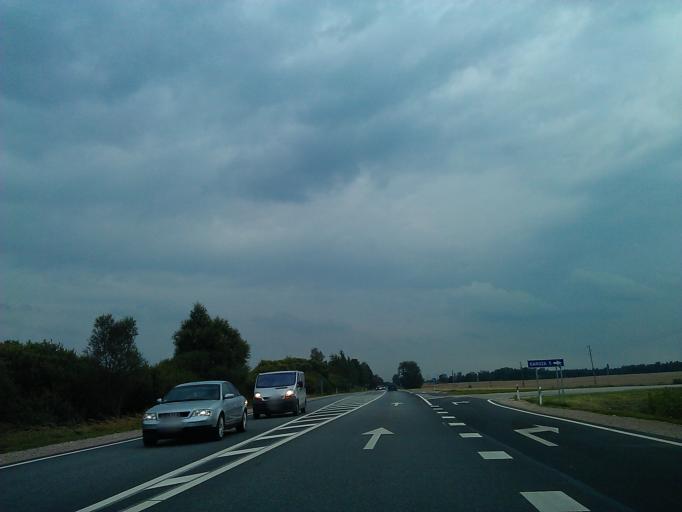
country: LV
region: Bauskas Rajons
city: Bauska
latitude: 56.5032
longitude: 24.1739
